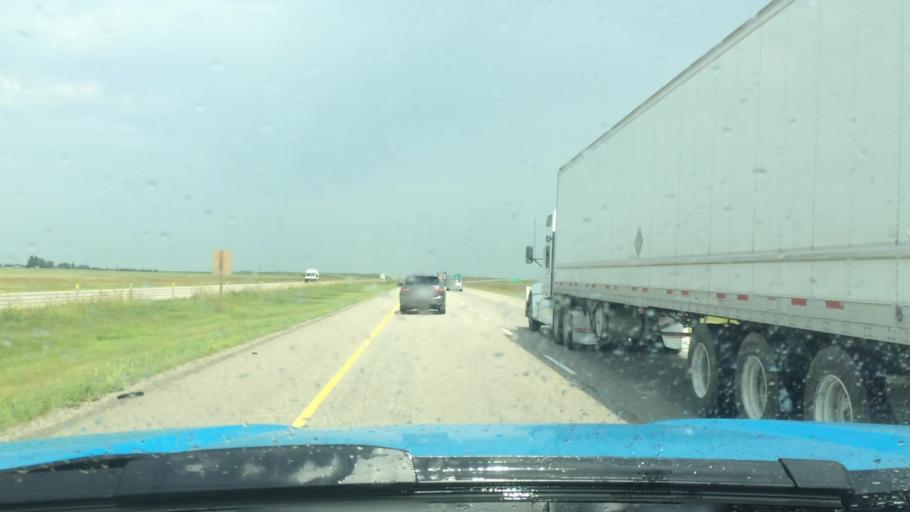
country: CA
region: Alberta
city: Didsbury
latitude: 51.6540
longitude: -114.0254
